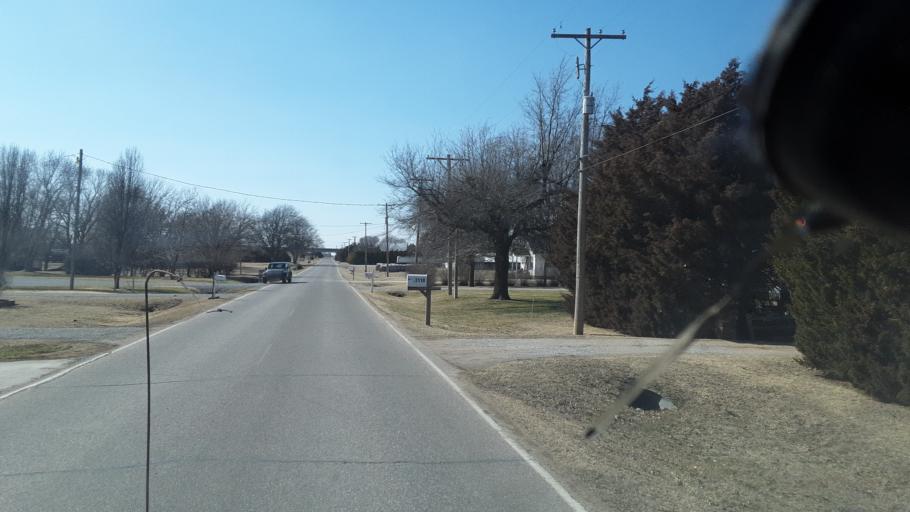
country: US
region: Kansas
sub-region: Reno County
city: Haven
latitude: 37.9410
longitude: -97.8749
